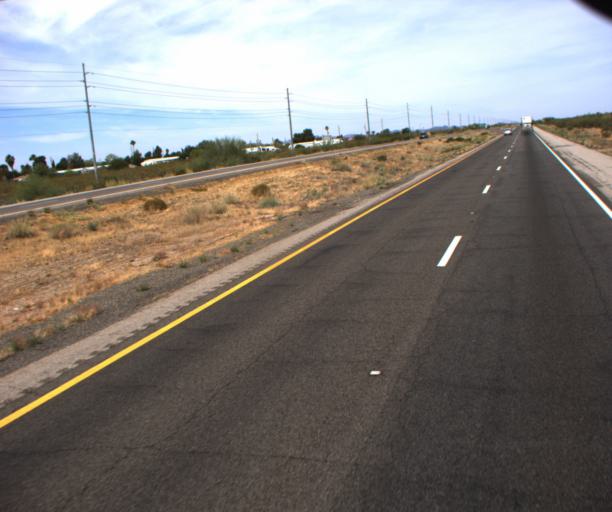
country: US
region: Arizona
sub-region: Maricopa County
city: Sun City West
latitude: 33.7863
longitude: -112.5393
